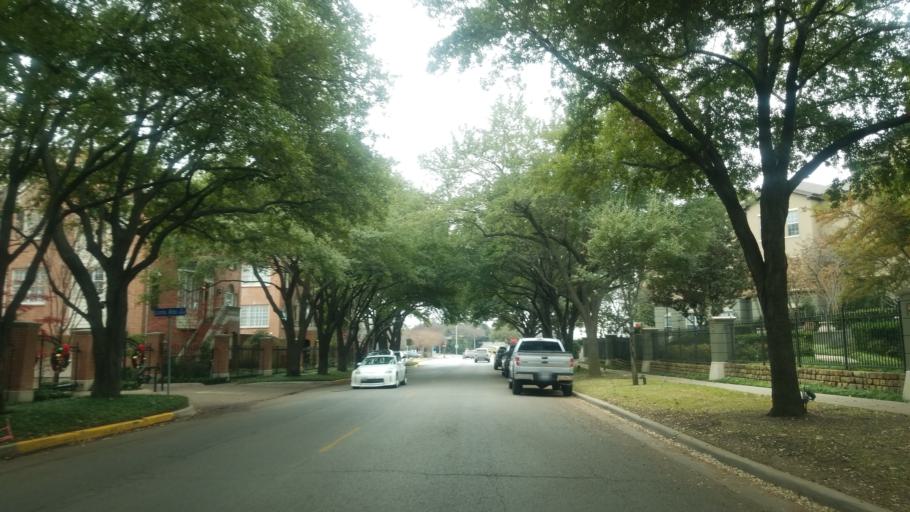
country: US
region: Texas
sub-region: Dallas County
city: Highland Park
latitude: 32.8219
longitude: -96.8140
